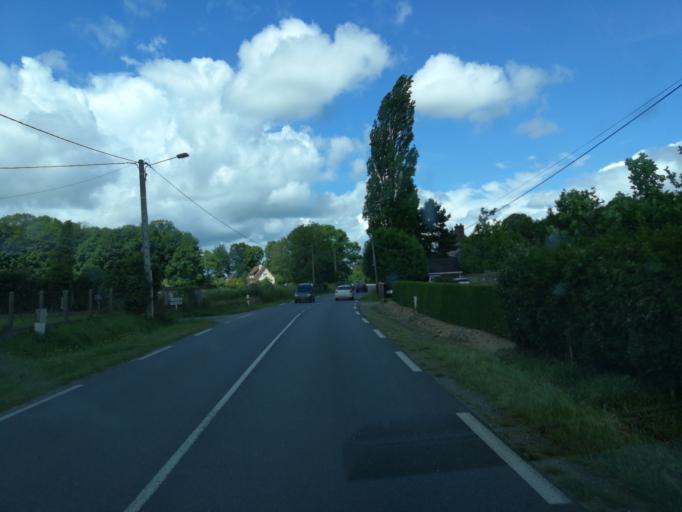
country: FR
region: Haute-Normandie
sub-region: Departement de l'Eure
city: Saint-Ouen-de-Thouberville
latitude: 49.3551
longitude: 0.8990
